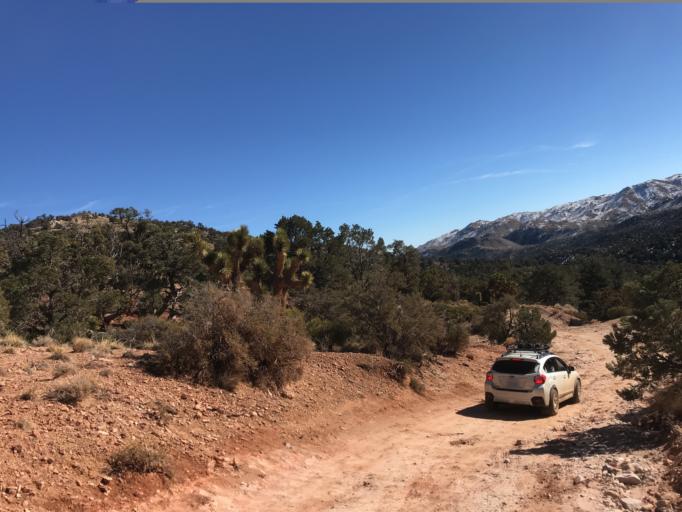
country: US
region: California
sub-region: San Bernardino County
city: Big Bear City
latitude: 34.2396
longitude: -116.6909
